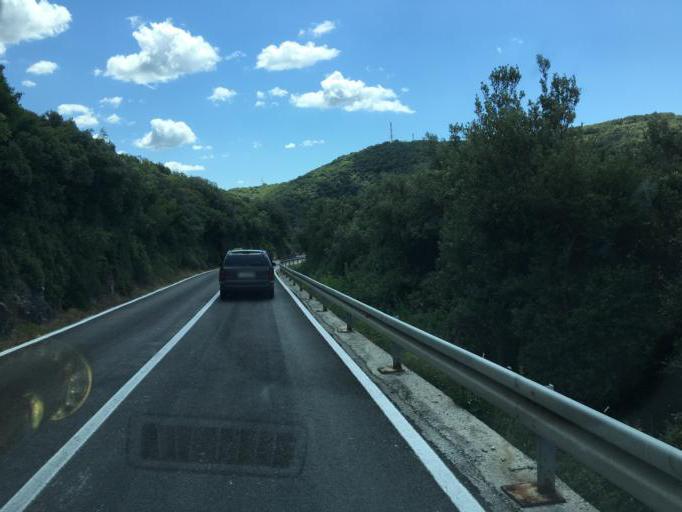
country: HR
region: Istarska
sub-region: Grad Rovinj
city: Rovinj
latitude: 45.1349
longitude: 13.7323
